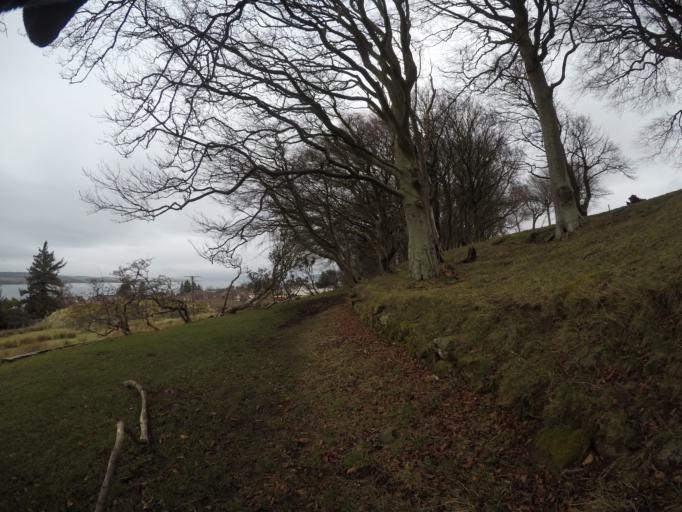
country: GB
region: Scotland
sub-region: North Ayrshire
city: Fairlie
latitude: 55.7562
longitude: -4.8496
